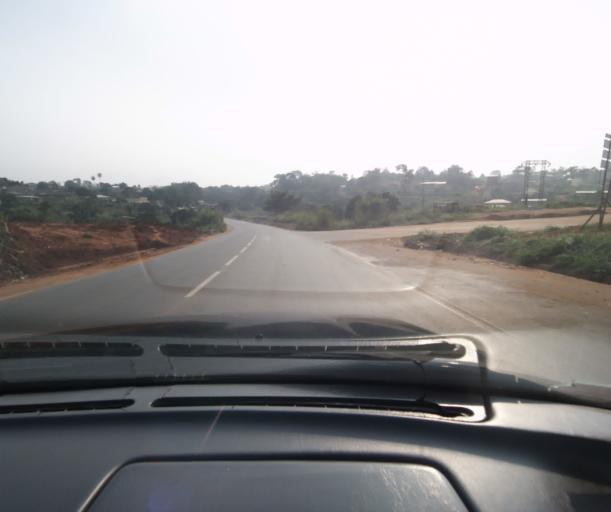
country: CM
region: Centre
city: Okoa
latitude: 3.9598
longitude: 11.5373
